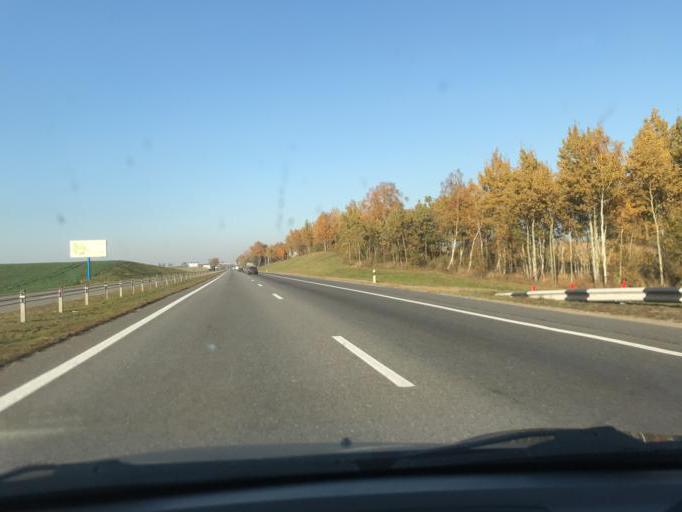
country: BY
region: Minsk
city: Samakhvalavichy
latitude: 53.7725
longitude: 27.5231
